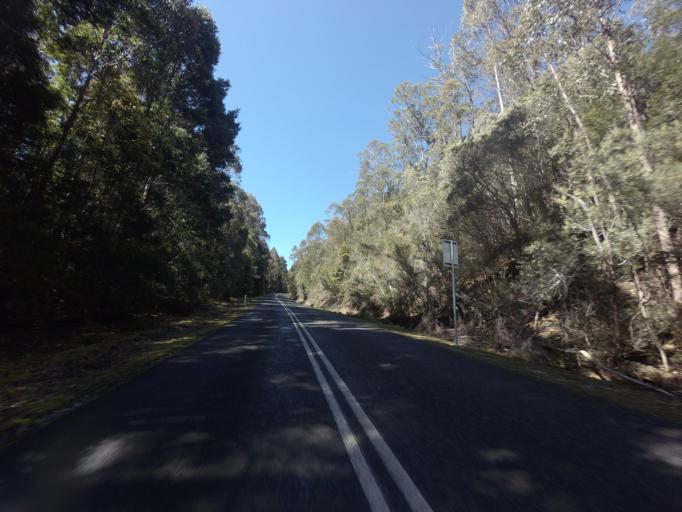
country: AU
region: Tasmania
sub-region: Derwent Valley
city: New Norfolk
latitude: -42.7231
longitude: 146.4363
